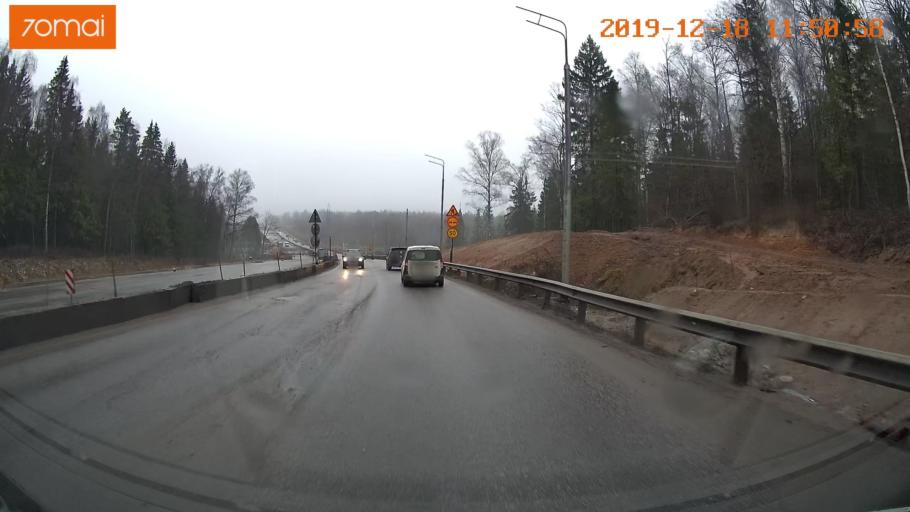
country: RU
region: Moskovskaya
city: Yershovo
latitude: 55.7899
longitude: 36.9216
